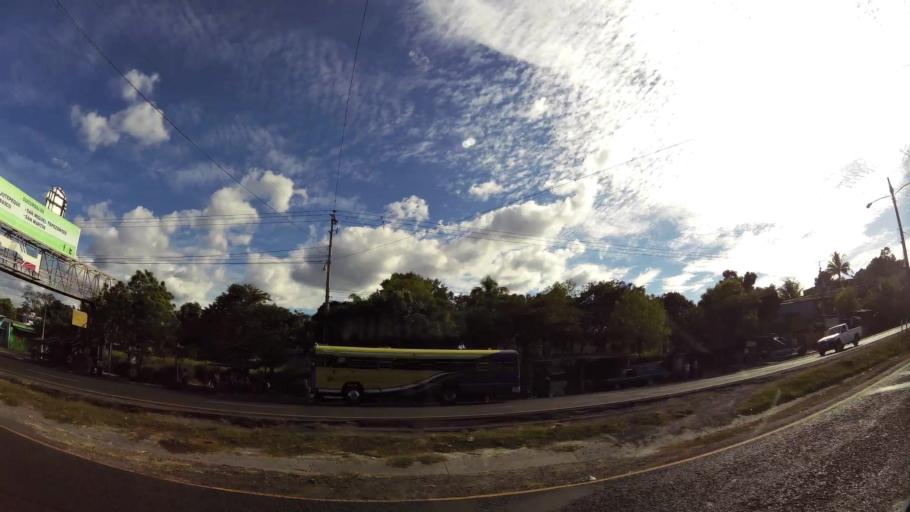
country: SV
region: San Salvador
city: Ilopango
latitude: 13.7342
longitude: -89.0624
